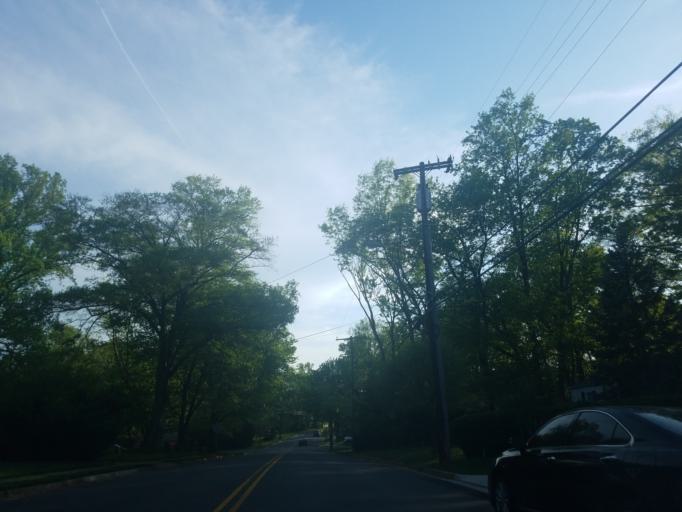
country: US
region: Virginia
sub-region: Fairfax County
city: Vienna
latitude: 38.8928
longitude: -77.2568
